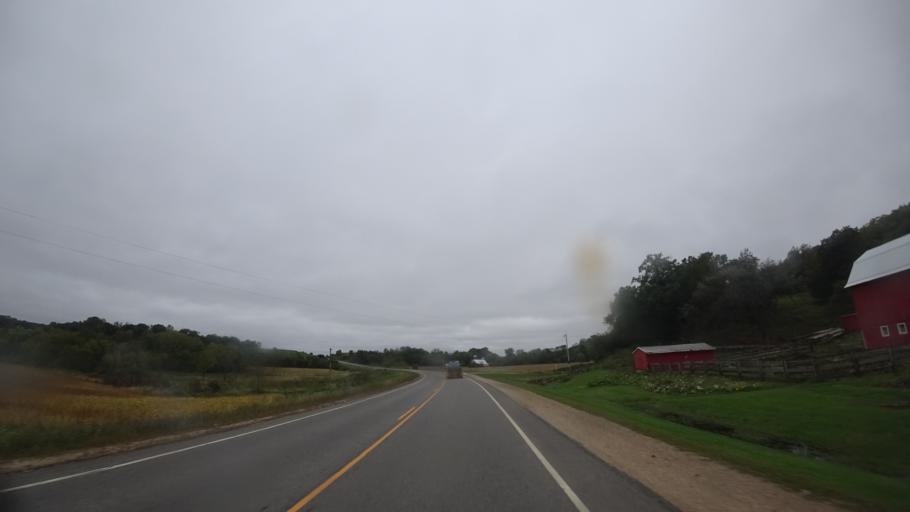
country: US
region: Wisconsin
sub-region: Crawford County
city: Prairie du Chien
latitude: 43.0253
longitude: -91.0262
